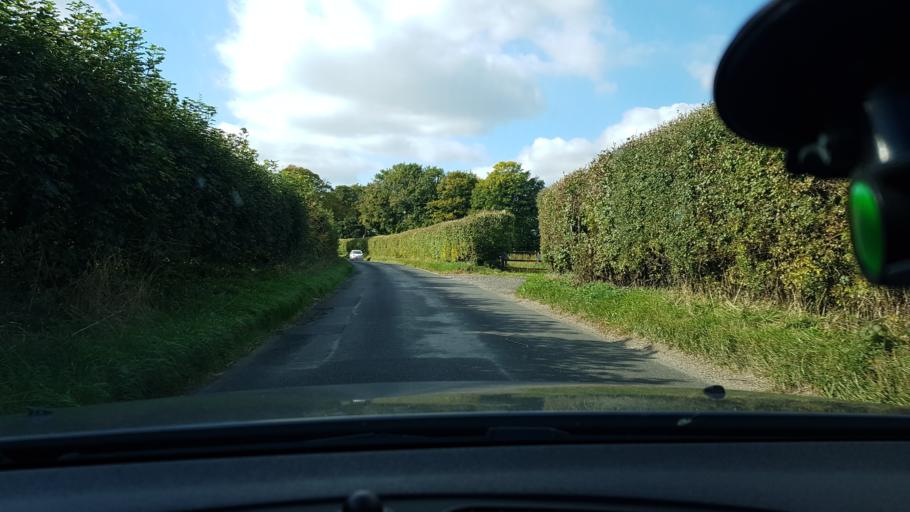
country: GB
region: England
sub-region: West Berkshire
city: Kintbury
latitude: 51.4010
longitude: -1.4614
